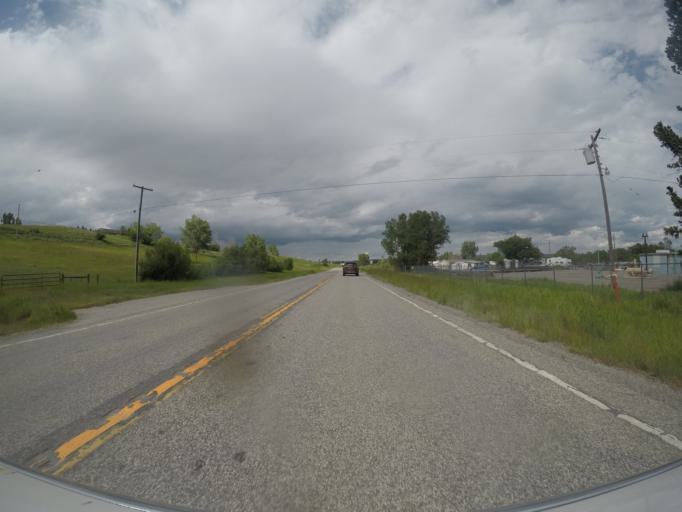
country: US
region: Montana
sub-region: Sweet Grass County
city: Big Timber
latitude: 45.8217
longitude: -109.9537
